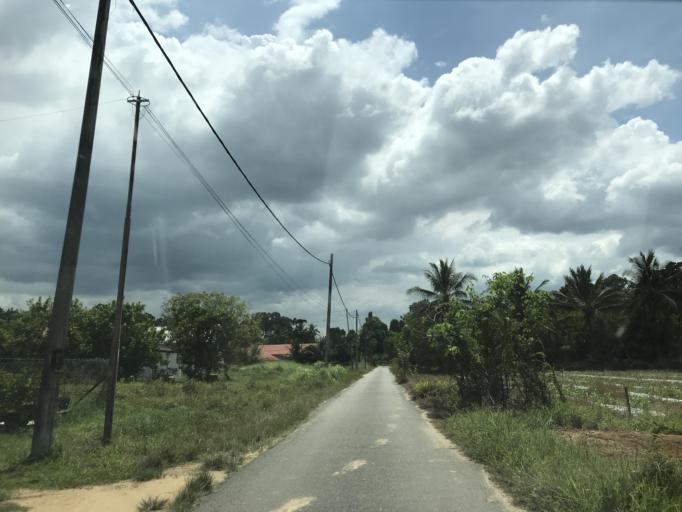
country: MY
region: Kelantan
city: Kota Bharu
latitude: 6.1123
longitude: 102.1830
